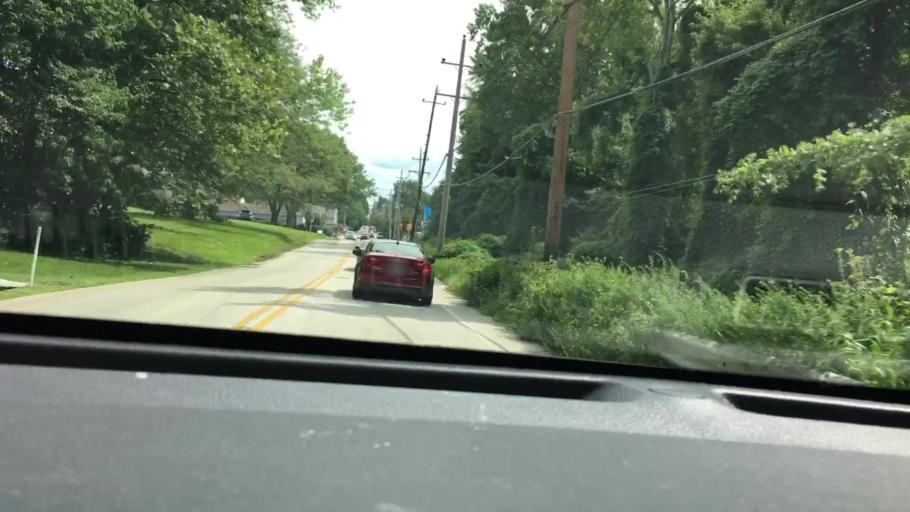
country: US
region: Pennsylvania
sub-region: Bucks County
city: Feasterville
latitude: 40.1301
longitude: -75.0265
